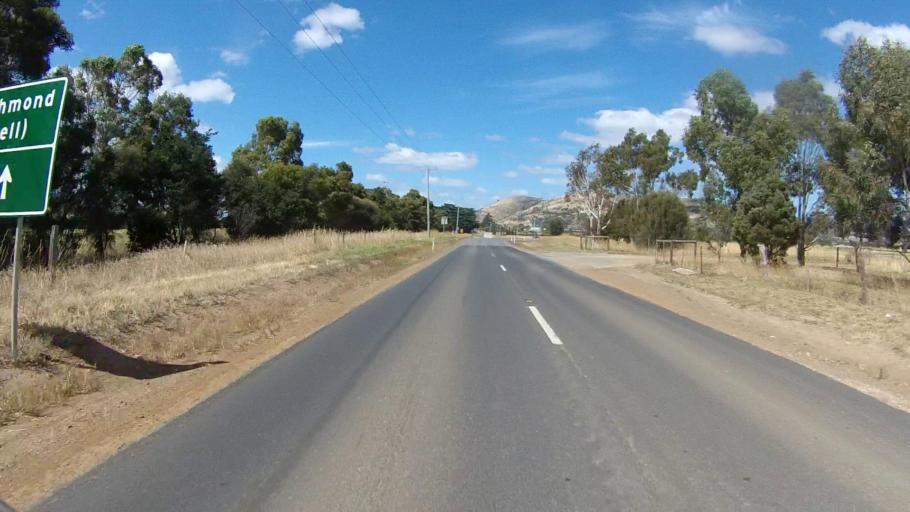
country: AU
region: Tasmania
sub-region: Clarence
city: Cambridge
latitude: -42.7269
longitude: 147.4358
